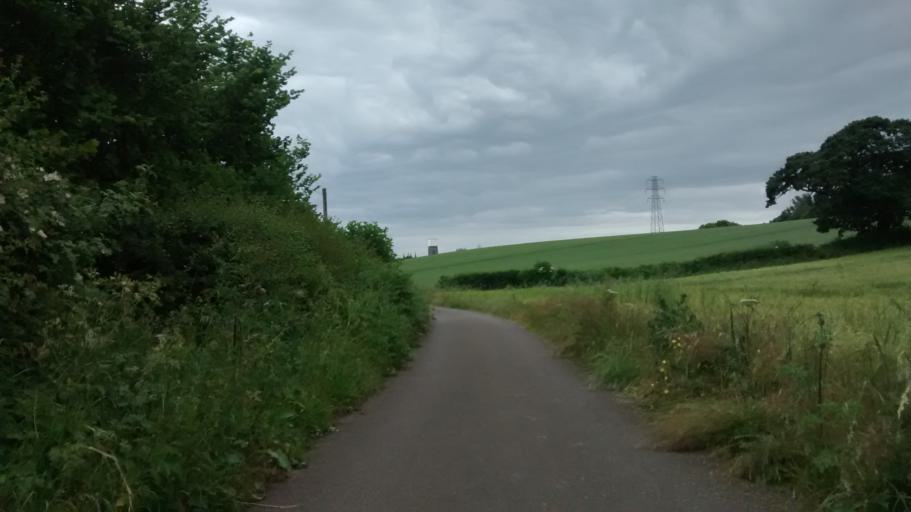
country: GB
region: England
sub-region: County Durham
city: Durham
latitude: 54.7891
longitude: -1.5649
